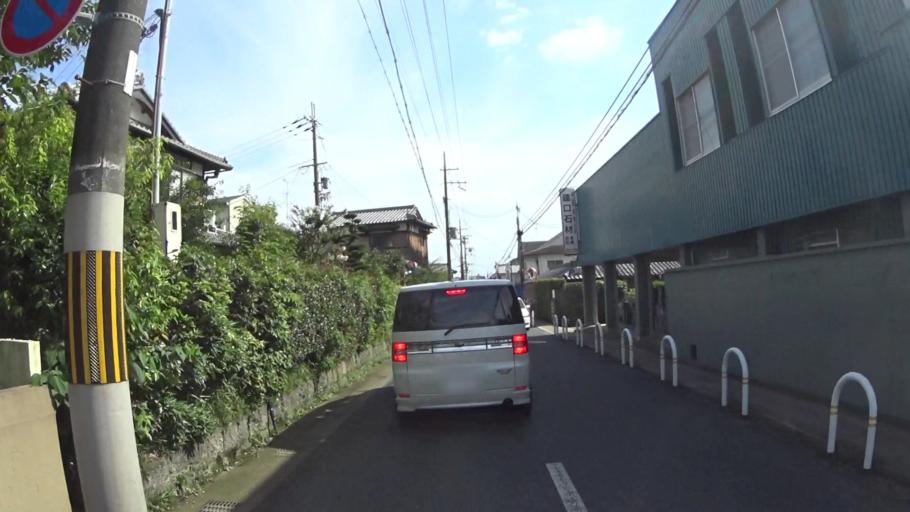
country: JP
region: Kyoto
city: Muko
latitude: 34.9562
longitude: 135.7003
